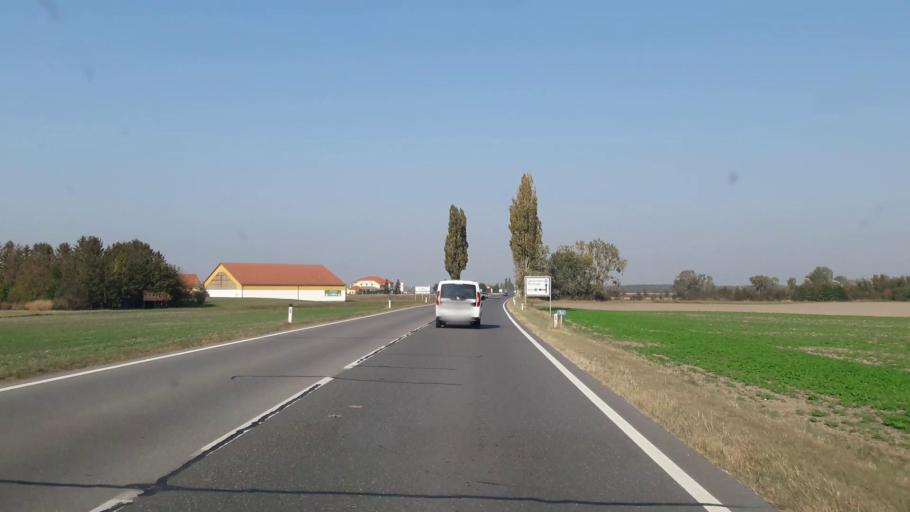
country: AT
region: Lower Austria
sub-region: Politischer Bezirk Ganserndorf
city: Engelhartstetten
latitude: 48.1807
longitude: 16.8921
